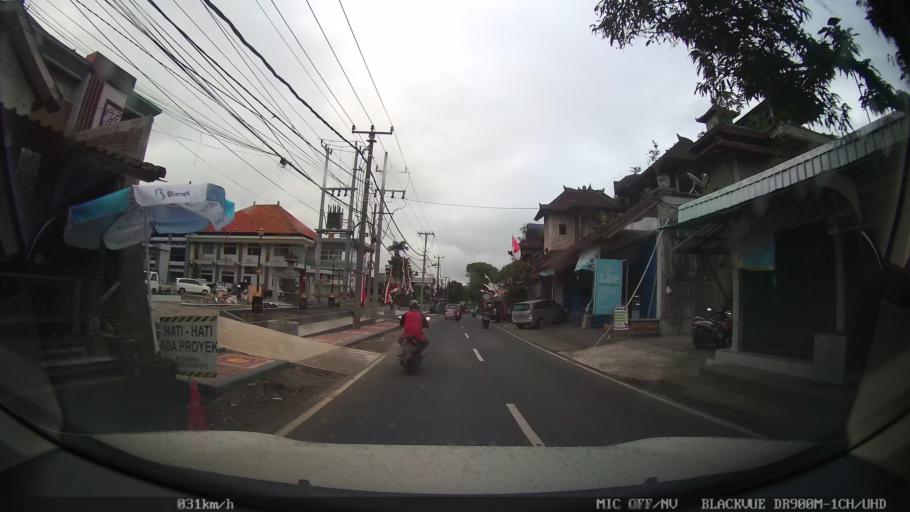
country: ID
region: Bali
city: Badung
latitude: -8.4214
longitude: 115.2451
